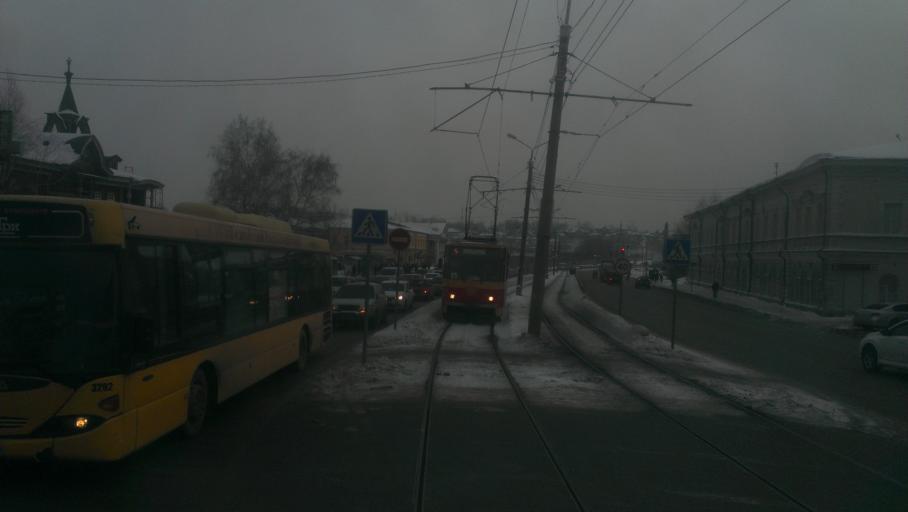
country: RU
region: Altai Krai
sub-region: Gorod Barnaulskiy
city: Barnaul
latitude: 53.3304
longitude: 83.7830
